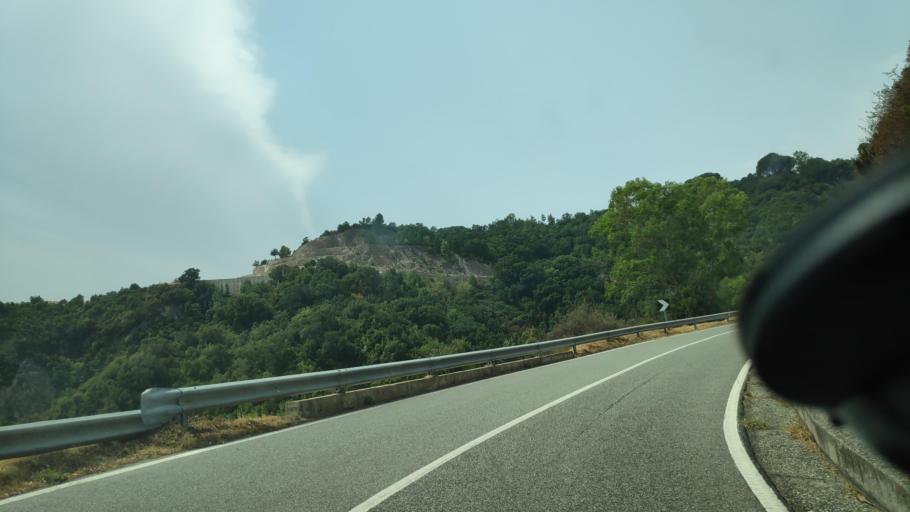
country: IT
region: Calabria
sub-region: Provincia di Catanzaro
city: San Sostene
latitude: 38.6402
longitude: 16.5126
